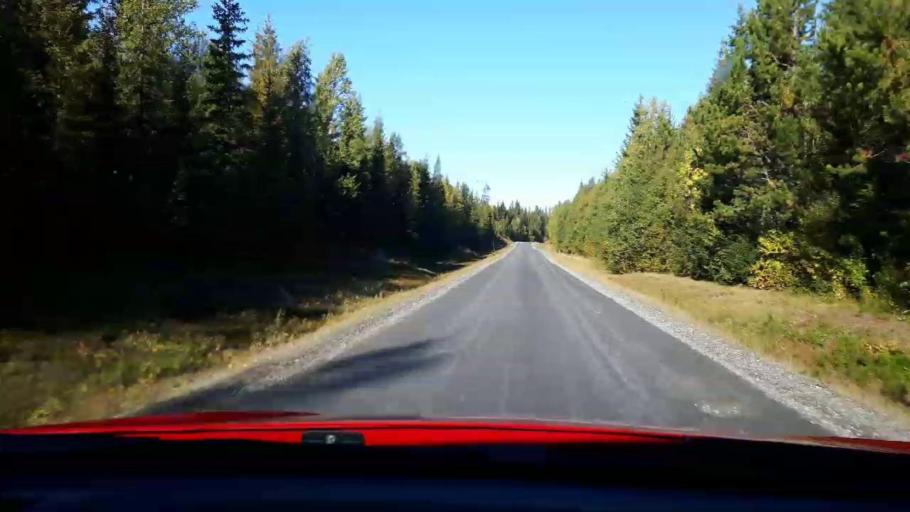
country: NO
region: Nord-Trondelag
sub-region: Lierne
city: Sandvika
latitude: 64.5291
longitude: 14.0474
